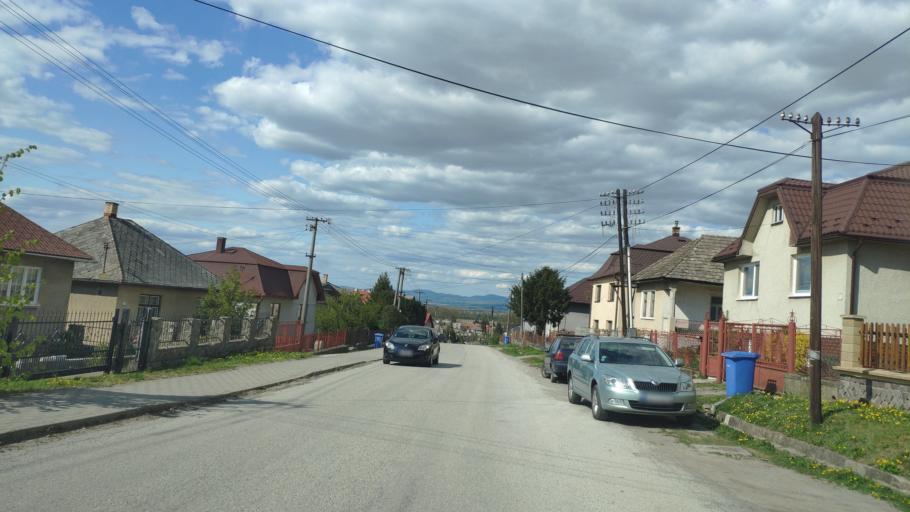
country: SK
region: Kosicky
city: Kosice
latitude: 48.6769
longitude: 21.4308
